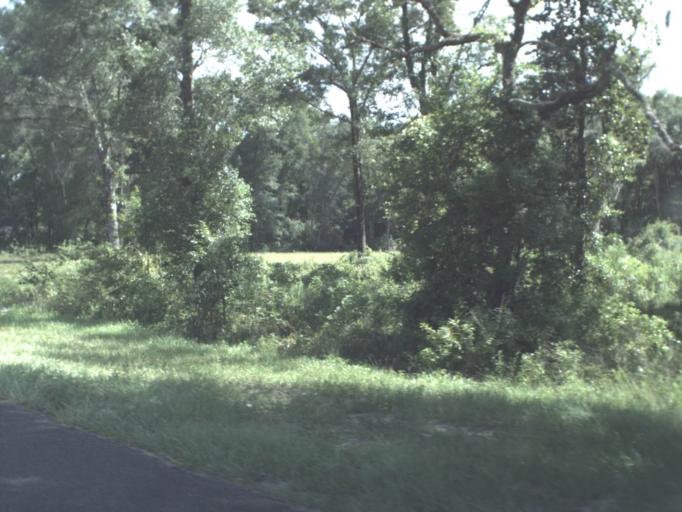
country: US
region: Florida
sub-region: Levy County
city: Manatee Road
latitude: 29.5353
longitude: -82.8909
